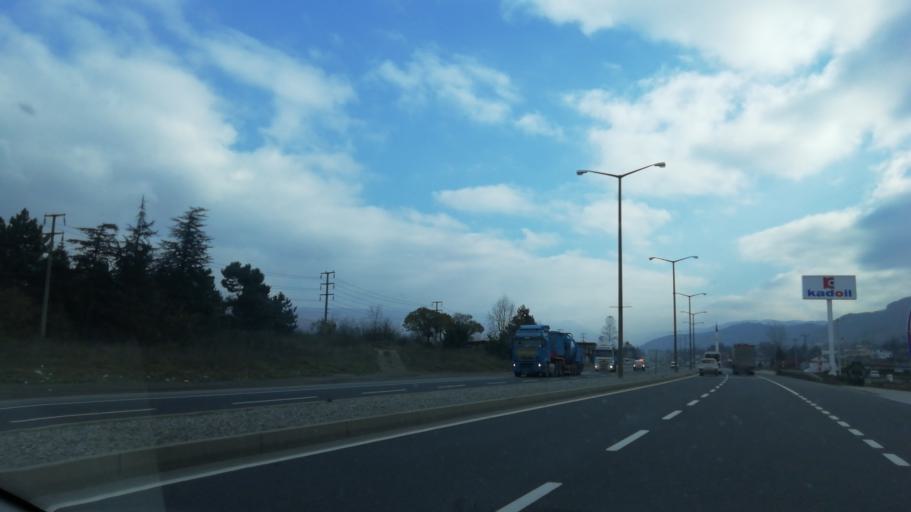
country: TR
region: Duzce
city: Kaynasli
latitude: 40.7796
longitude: 31.2842
